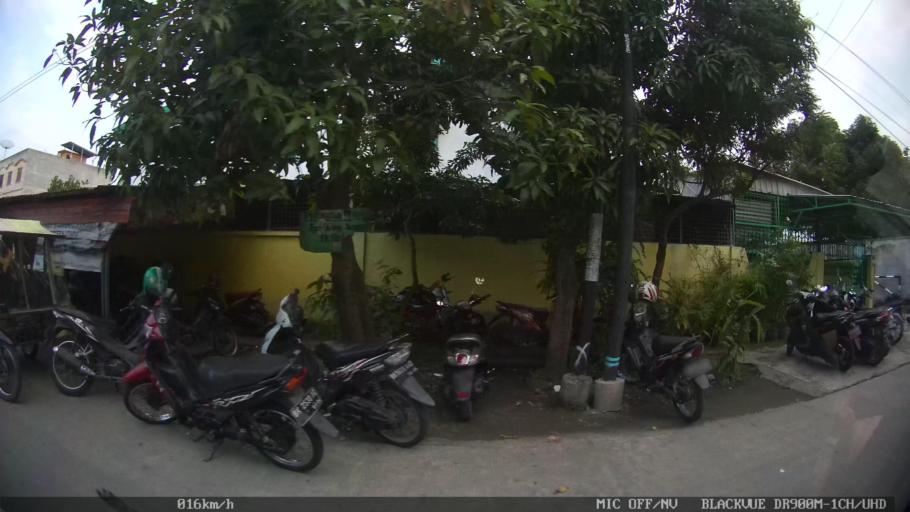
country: ID
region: North Sumatra
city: Medan
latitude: 3.6071
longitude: 98.6813
